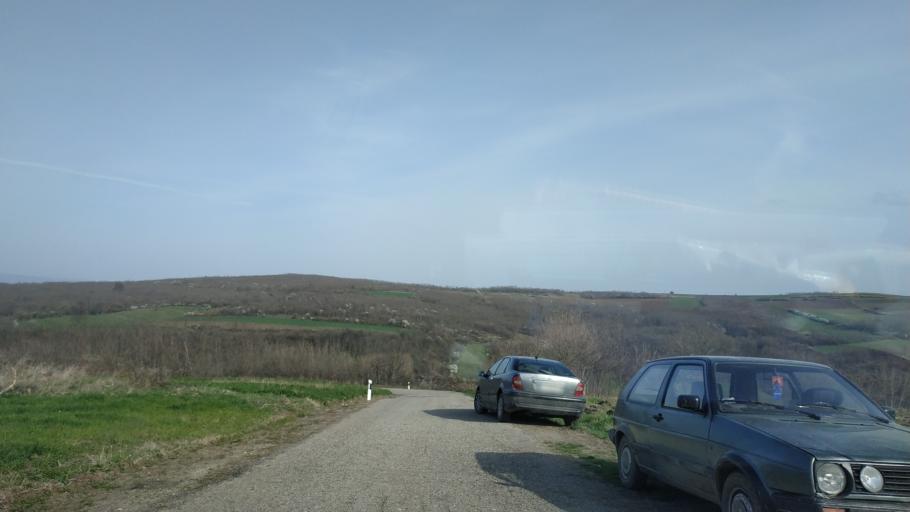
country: RS
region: Central Serbia
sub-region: Nisavski Okrug
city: Aleksinac
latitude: 43.5011
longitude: 21.6385
